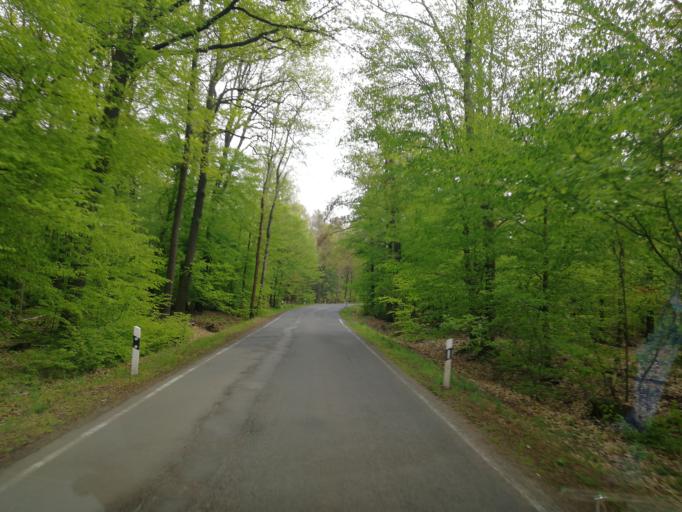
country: DE
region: Brandenburg
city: Herzberg
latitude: 51.6448
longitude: 13.1650
